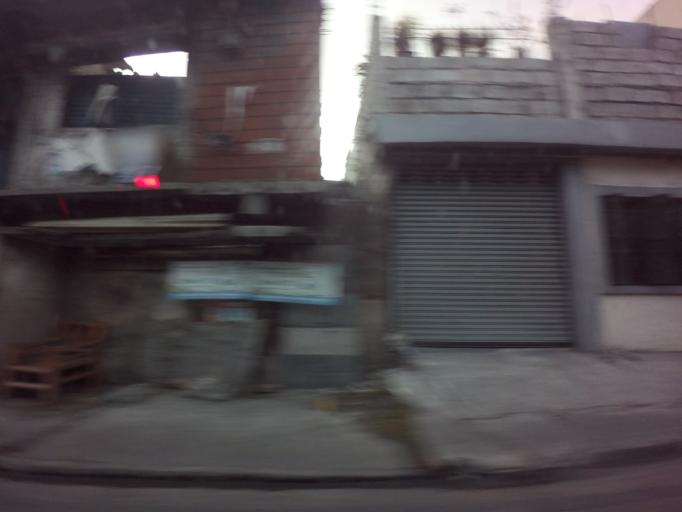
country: PH
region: Metro Manila
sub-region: Mandaluyong
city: Mandaluyong City
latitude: 14.5666
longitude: 121.0471
